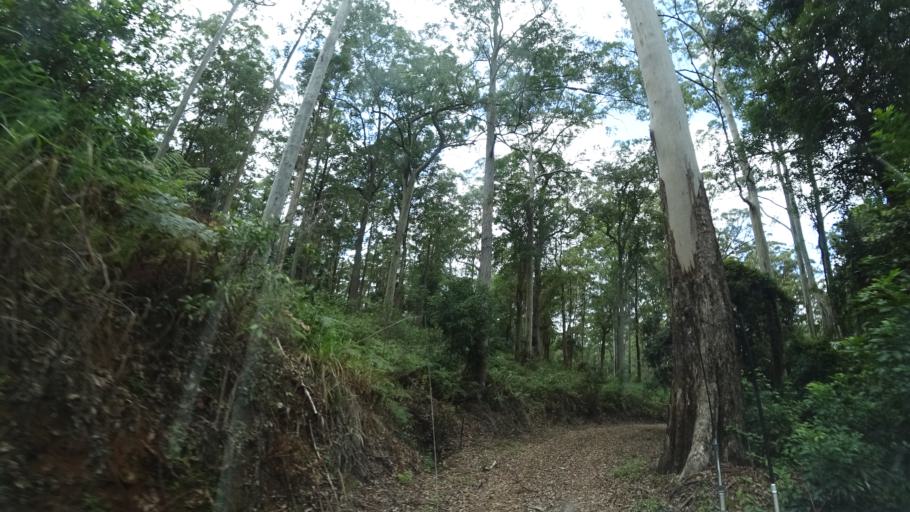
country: AU
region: Queensland
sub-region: Moreton Bay
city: Highvale
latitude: -27.4035
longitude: 152.7762
